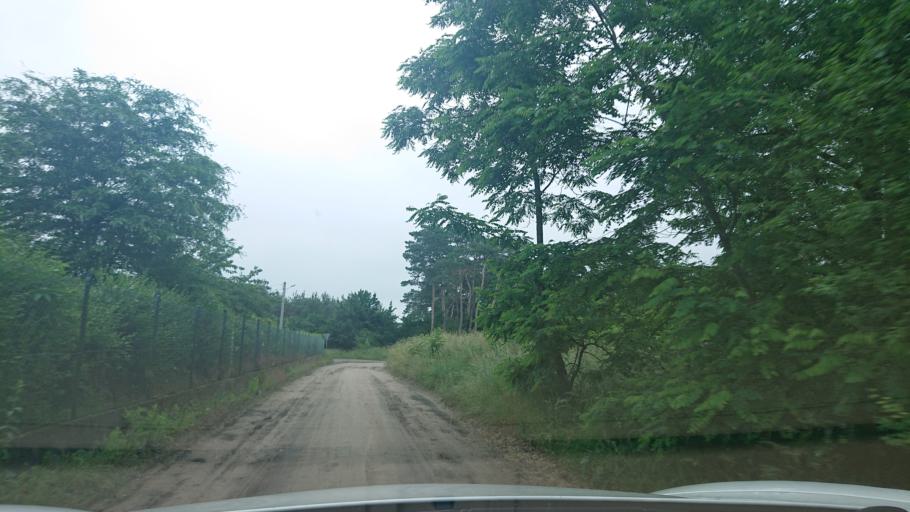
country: PL
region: Greater Poland Voivodeship
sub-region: Powiat gnieznienski
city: Gniezno
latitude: 52.5079
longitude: 17.5987
